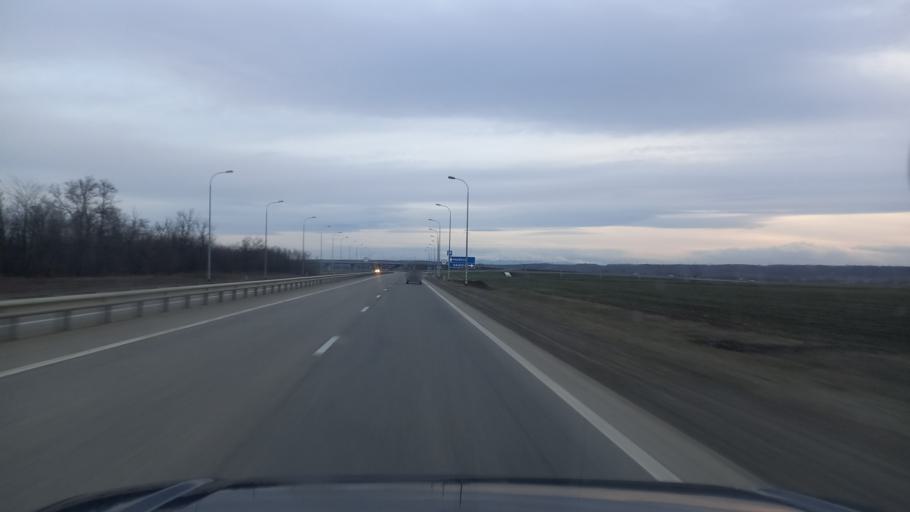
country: RU
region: Adygeya
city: Khanskaya
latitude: 44.6653
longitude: 39.9932
